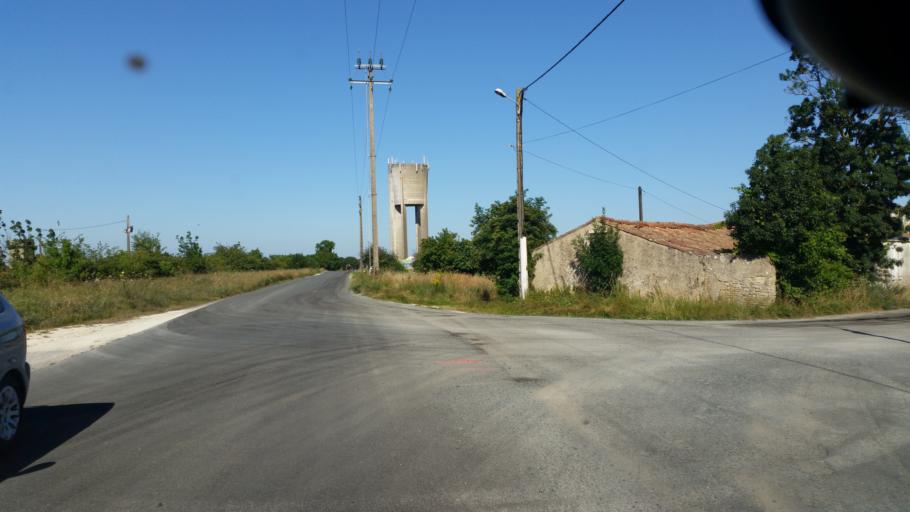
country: FR
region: Poitou-Charentes
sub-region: Departement de la Charente-Maritime
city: Marans
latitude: 46.3014
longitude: -0.9879
